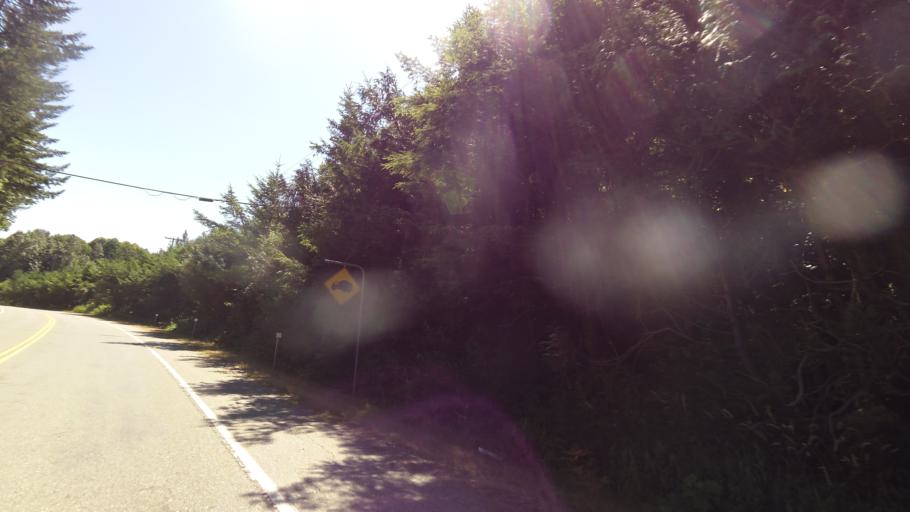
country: CA
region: British Columbia
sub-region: Fraser Valley Regional District
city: Chilliwack
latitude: 49.2265
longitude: -122.0160
